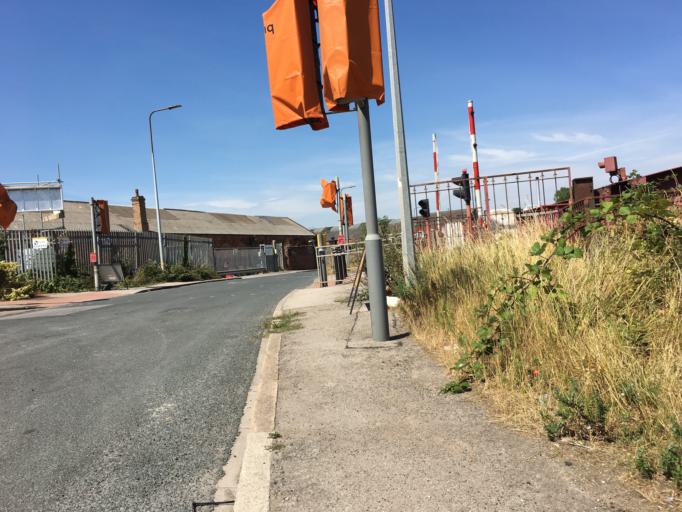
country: GB
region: England
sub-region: City of Kingston upon Hull
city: Hull
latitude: 53.7586
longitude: -0.3363
